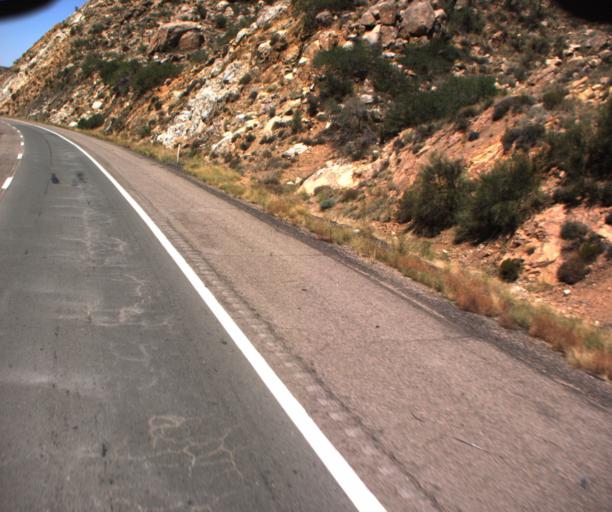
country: US
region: Arizona
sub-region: Mohave County
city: Peach Springs
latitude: 35.1738
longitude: -113.5063
